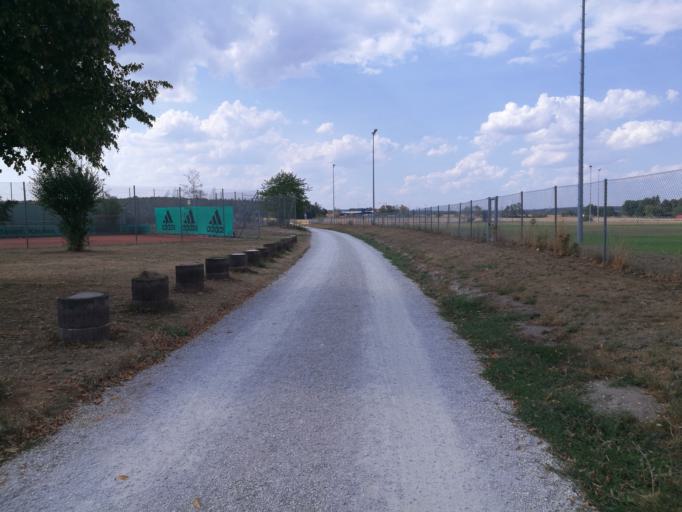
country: DE
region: Bavaria
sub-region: Regierungsbezirk Mittelfranken
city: Seukendorf
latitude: 49.4926
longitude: 10.9082
